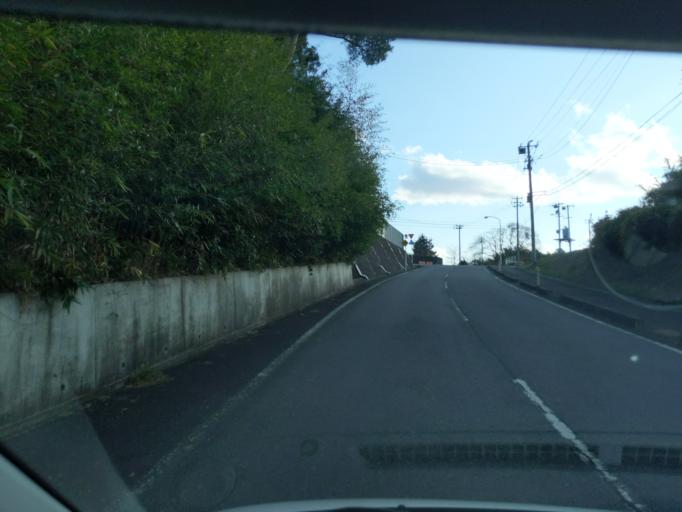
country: JP
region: Miyagi
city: Wakuya
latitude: 38.7005
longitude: 141.1580
